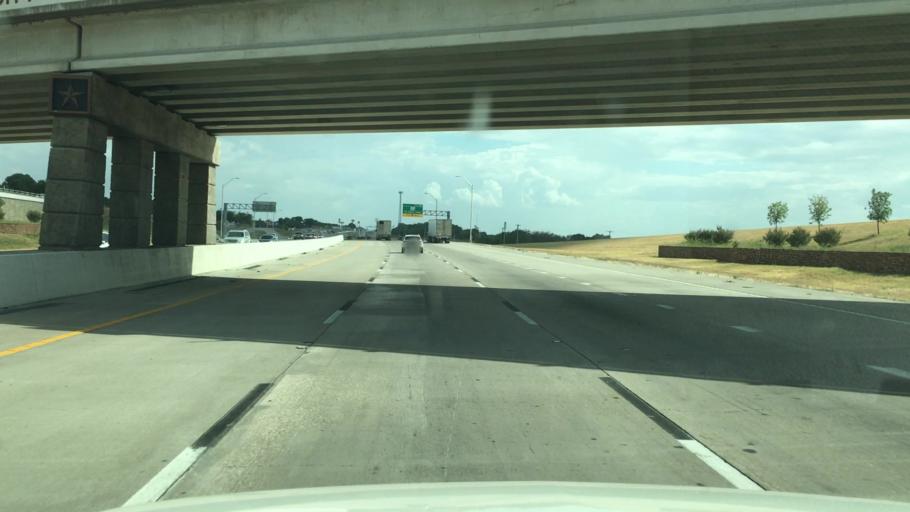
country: US
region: Texas
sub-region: McLennan County
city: West
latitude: 31.8193
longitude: -97.0981
